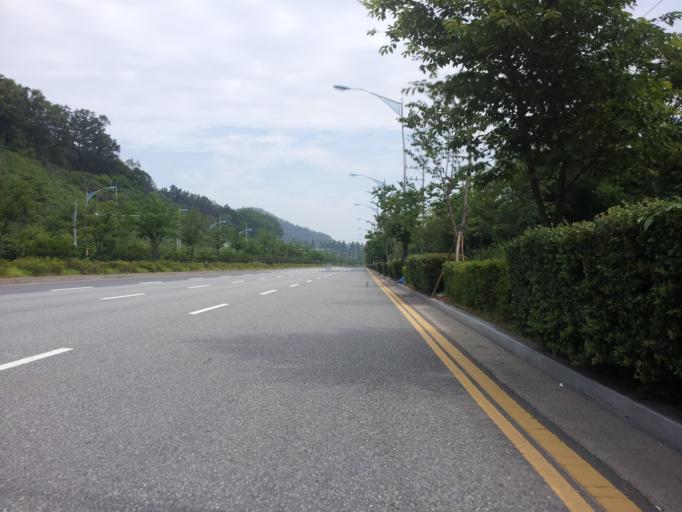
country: KR
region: Daejeon
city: Daejeon
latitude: 36.3265
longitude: 127.4735
